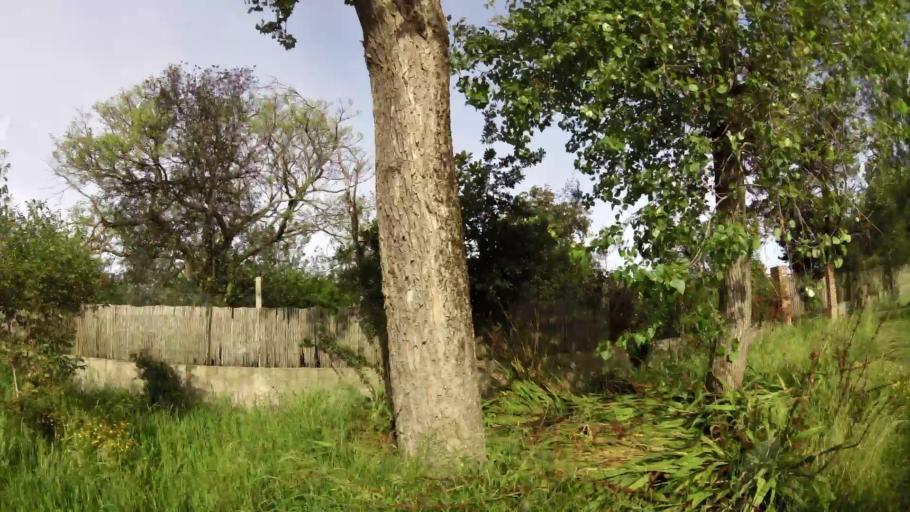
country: UY
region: Canelones
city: Atlantida
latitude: -34.7797
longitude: -55.8402
